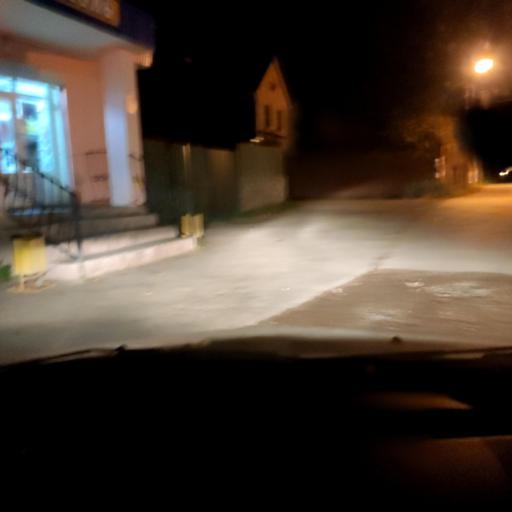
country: RU
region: Bashkortostan
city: Mikhaylovka
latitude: 54.8022
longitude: 55.9411
